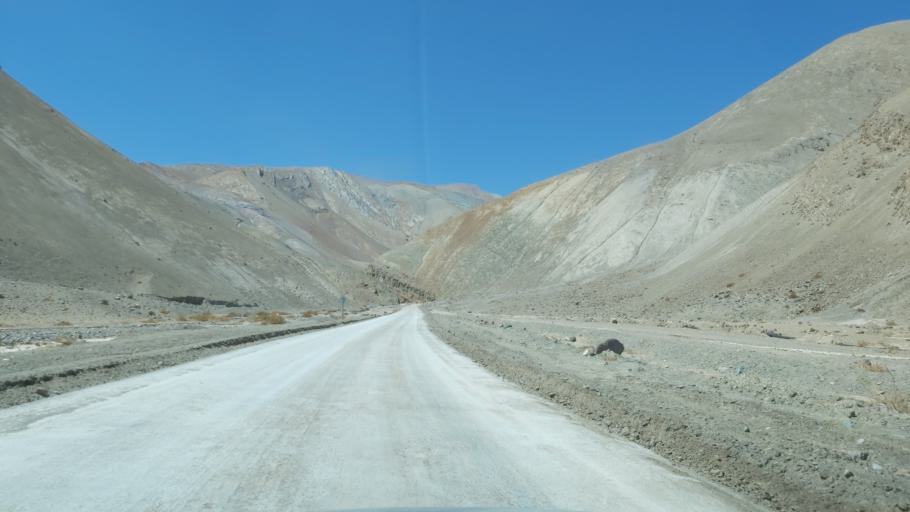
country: CL
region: Atacama
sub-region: Provincia de Chanaral
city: Diego de Almagro
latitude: -26.3991
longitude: -69.3801
